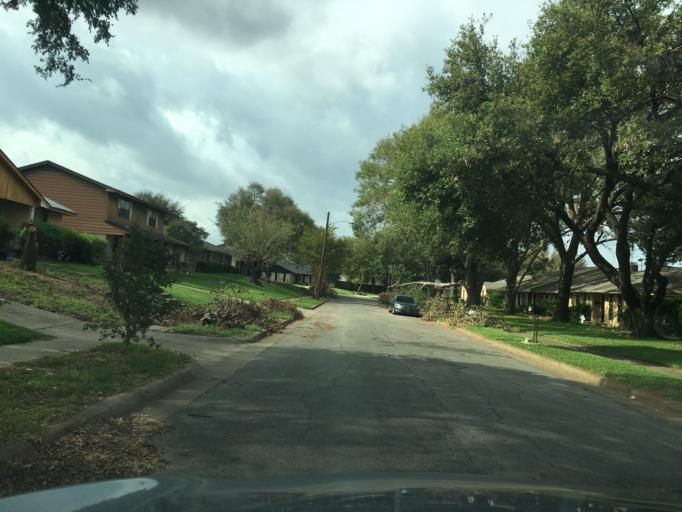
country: US
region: Texas
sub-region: Dallas County
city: Richardson
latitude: 32.9019
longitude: -96.7631
